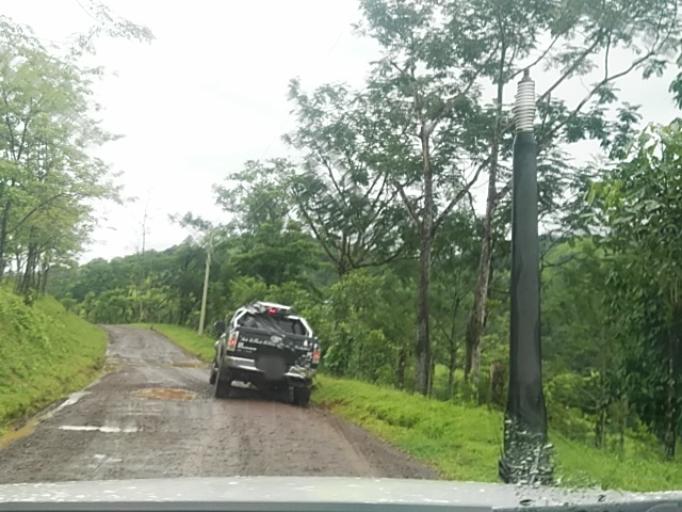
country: NI
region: Matagalpa
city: Rio Blanco
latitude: 13.0053
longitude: -85.2034
